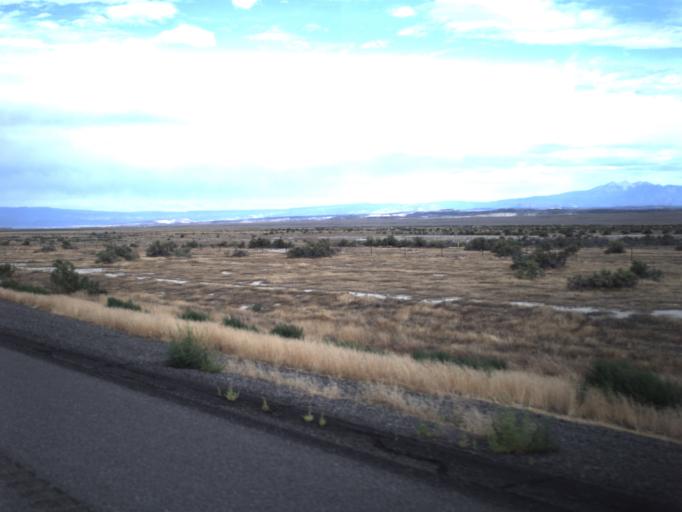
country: US
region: Utah
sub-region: Grand County
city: Moab
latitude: 38.9418
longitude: -109.5888
